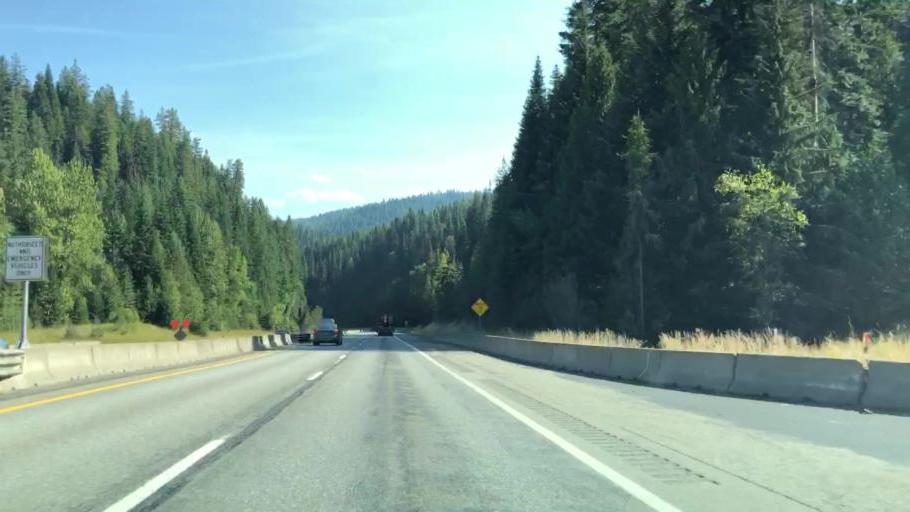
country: US
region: Idaho
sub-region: Shoshone County
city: Pinehurst
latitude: 47.6025
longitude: -116.4989
